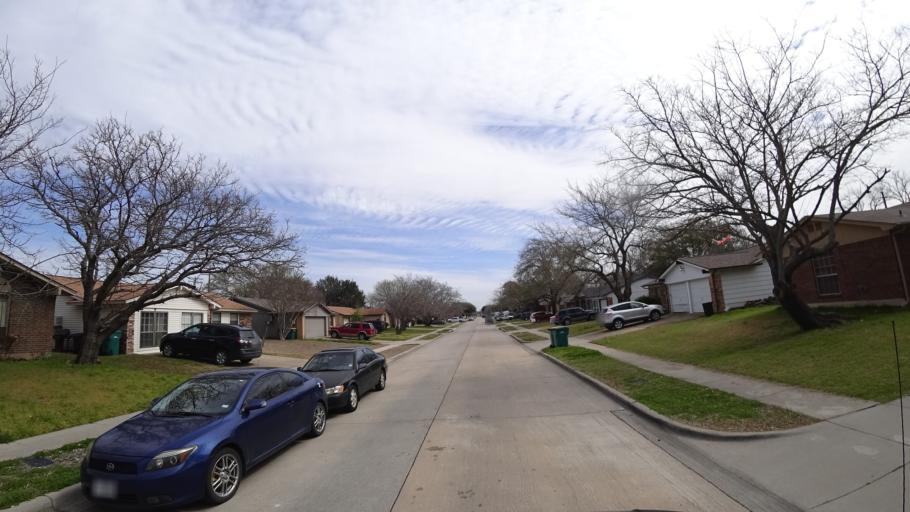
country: US
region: Texas
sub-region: Denton County
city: Lewisville
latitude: 33.0387
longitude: -97.0183
